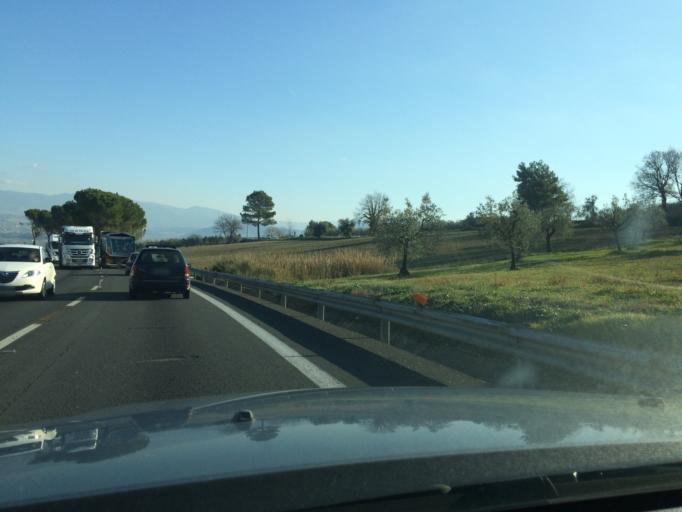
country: IT
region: Umbria
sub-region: Provincia di Terni
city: Narni Scalo
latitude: 42.5402
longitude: 12.5013
